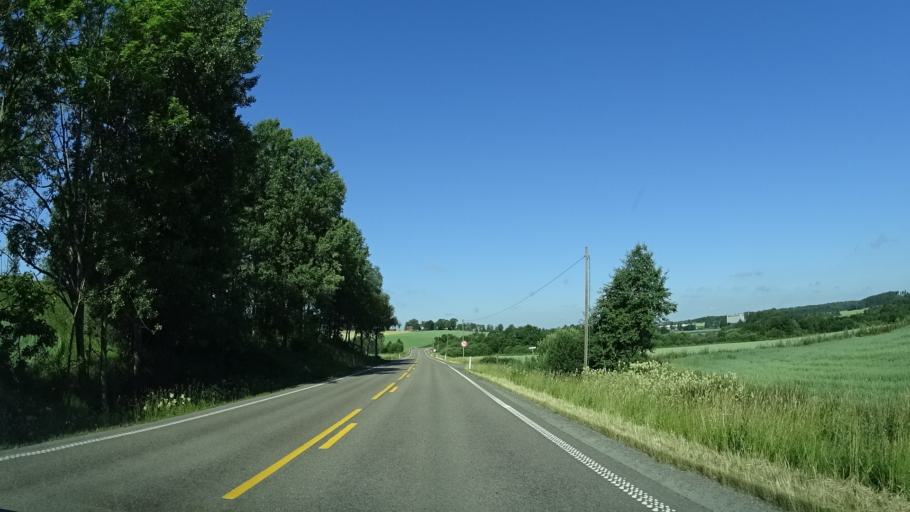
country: NO
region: Akershus
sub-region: Ski
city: Ski
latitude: 59.6848
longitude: 10.8363
